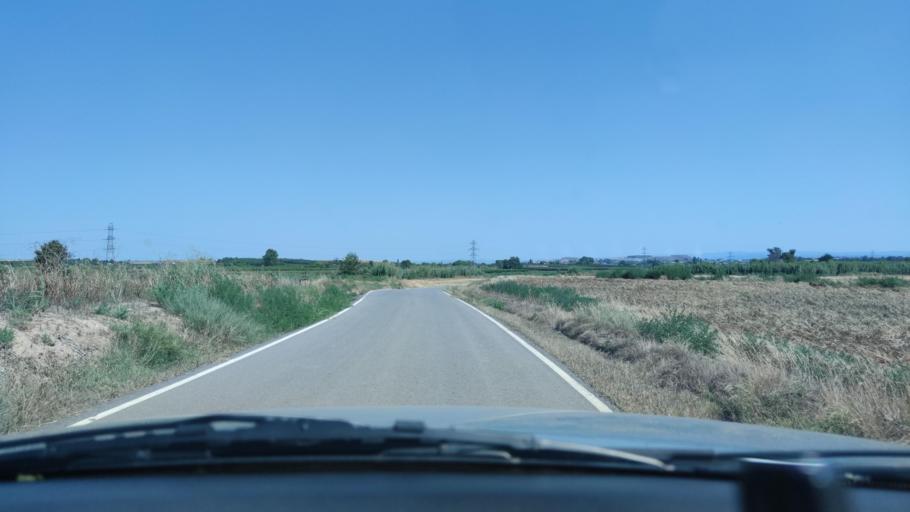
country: ES
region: Catalonia
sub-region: Provincia de Lleida
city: Torrefarrera
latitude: 41.6749
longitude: 0.6499
